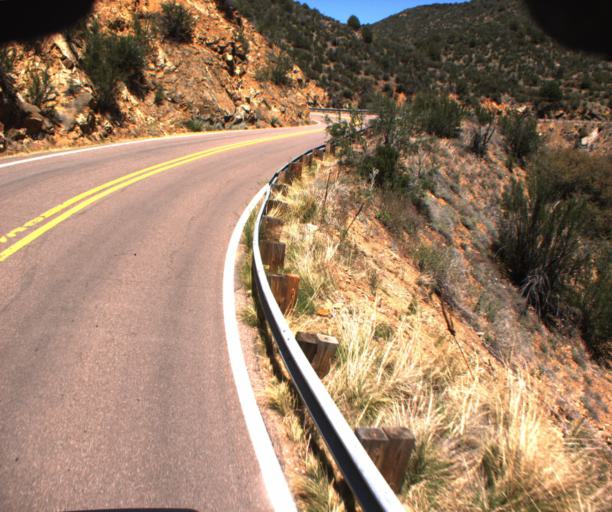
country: US
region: Arizona
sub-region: Yavapai County
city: Prescott
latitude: 34.4656
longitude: -112.5205
